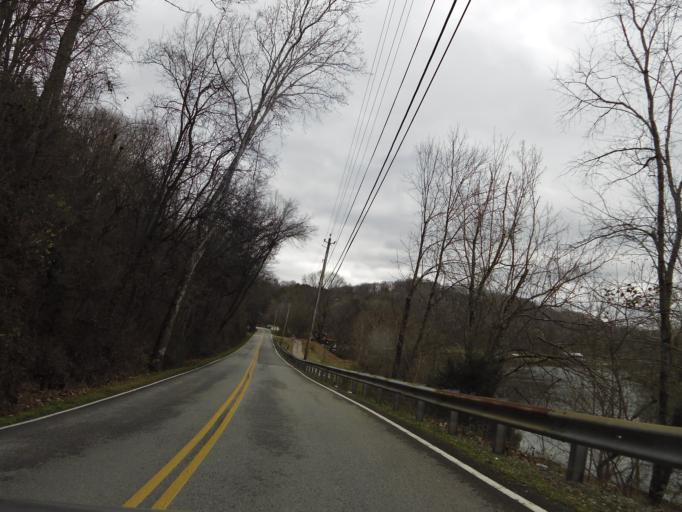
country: US
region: Tennessee
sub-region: Grainger County
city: Blaine
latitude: 36.1447
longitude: -83.6381
